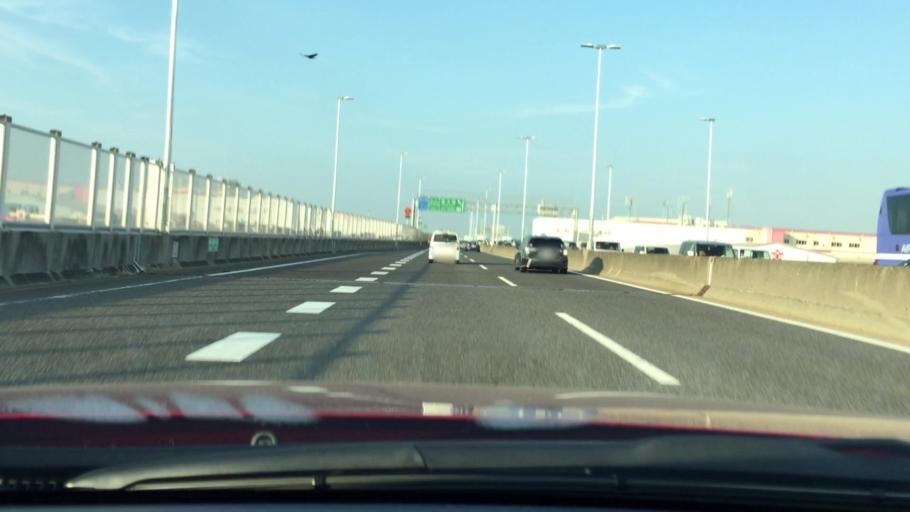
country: JP
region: Osaka
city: Takaishi
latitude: 34.5161
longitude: 135.4157
